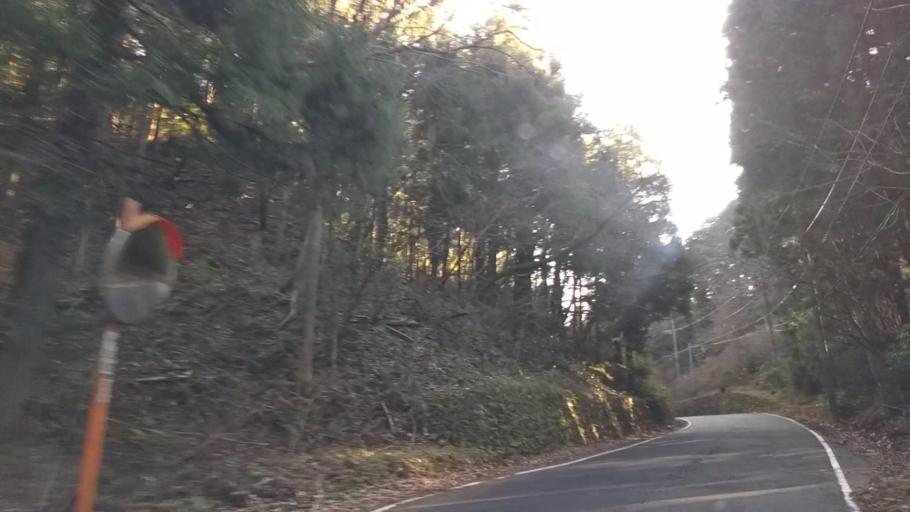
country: JP
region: Yamanashi
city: Uenohara
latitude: 35.5558
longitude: 139.2110
